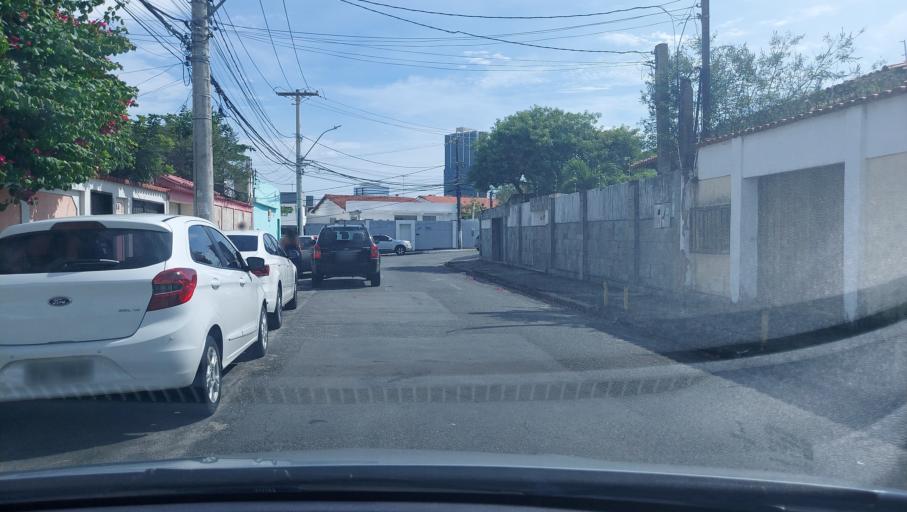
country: BR
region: Bahia
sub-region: Salvador
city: Salvador
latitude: -12.9822
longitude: -38.4460
